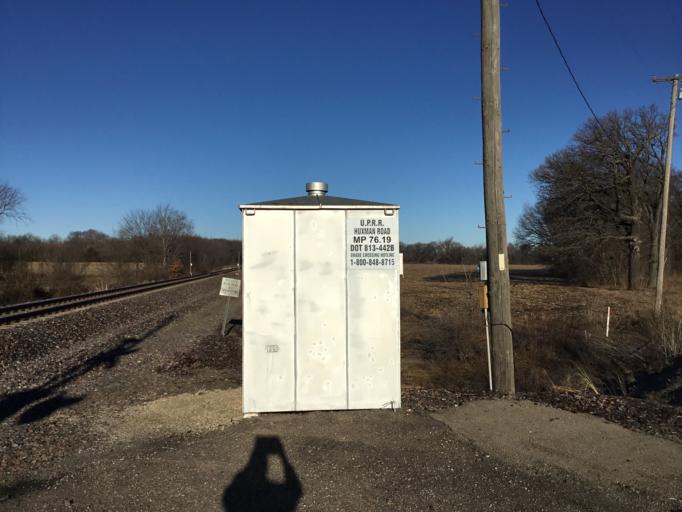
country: US
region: Kansas
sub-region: Shawnee County
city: Silver Lake
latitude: 39.1243
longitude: -95.7978
